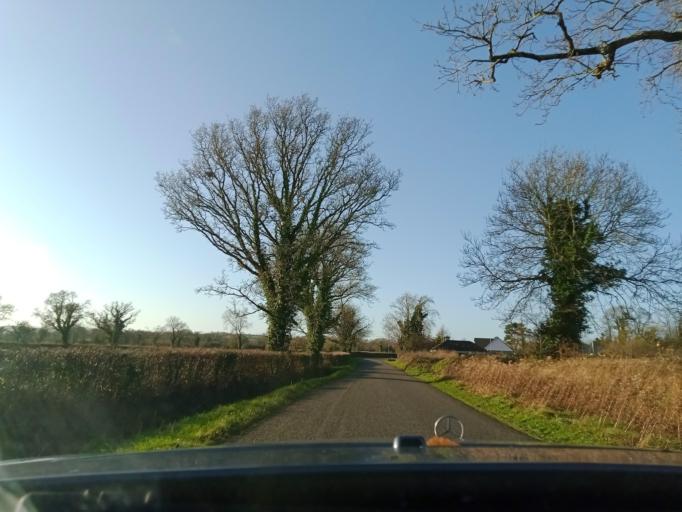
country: IE
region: Leinster
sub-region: Kilkenny
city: Callan
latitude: 52.5013
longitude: -7.3636
